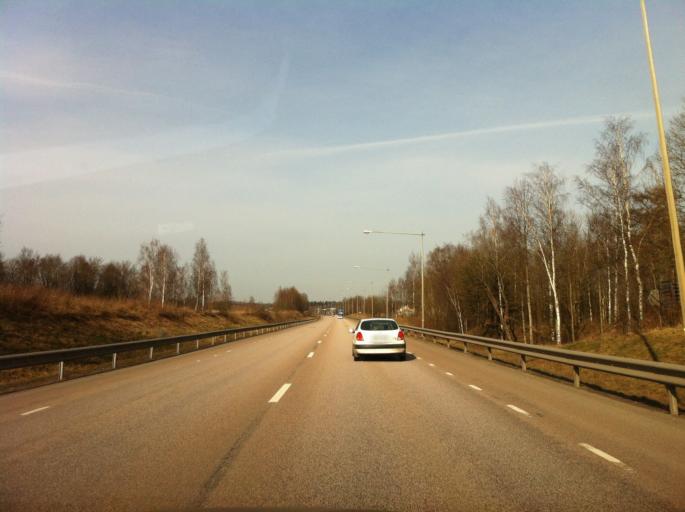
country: SE
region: Vaestra Goetaland
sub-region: Skovde Kommun
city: Skoevde
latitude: 58.3863
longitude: 13.8750
